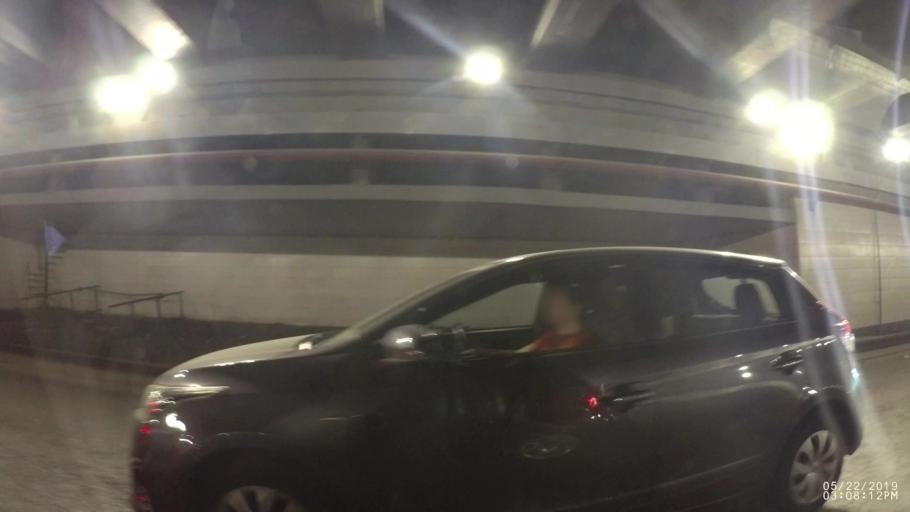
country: LB
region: Beyrouth
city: Beirut
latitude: 33.8859
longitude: 35.4980
